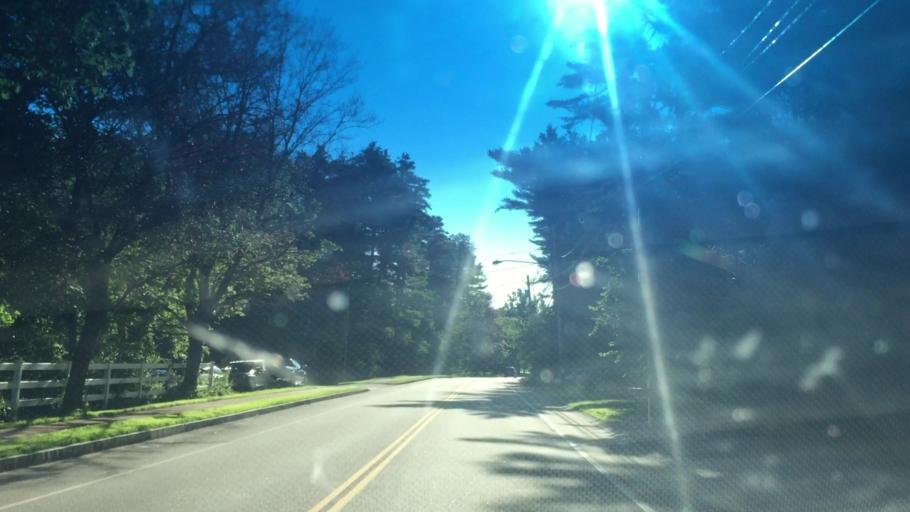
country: US
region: Massachusetts
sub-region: Norfolk County
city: Norfolk
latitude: 42.1204
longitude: -71.3204
